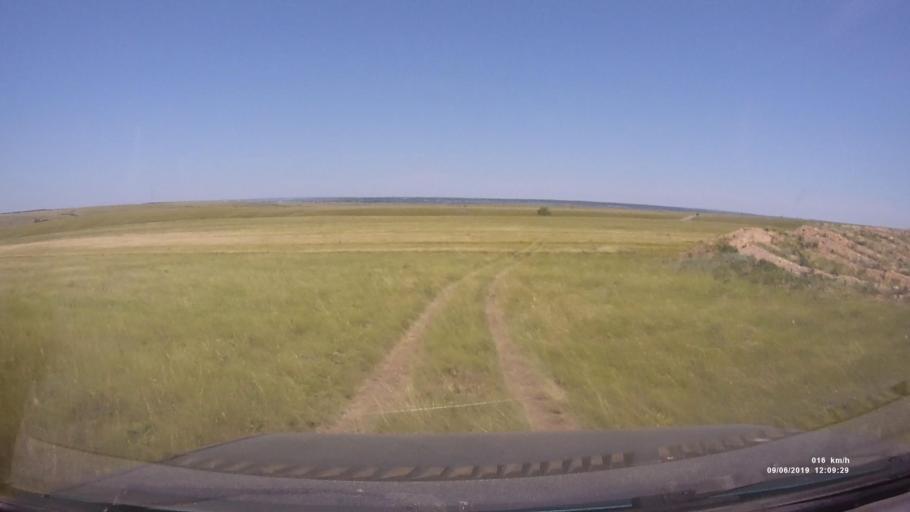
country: RU
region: Rostov
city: Staraya Stanitsa
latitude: 48.2480
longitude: 40.3380
